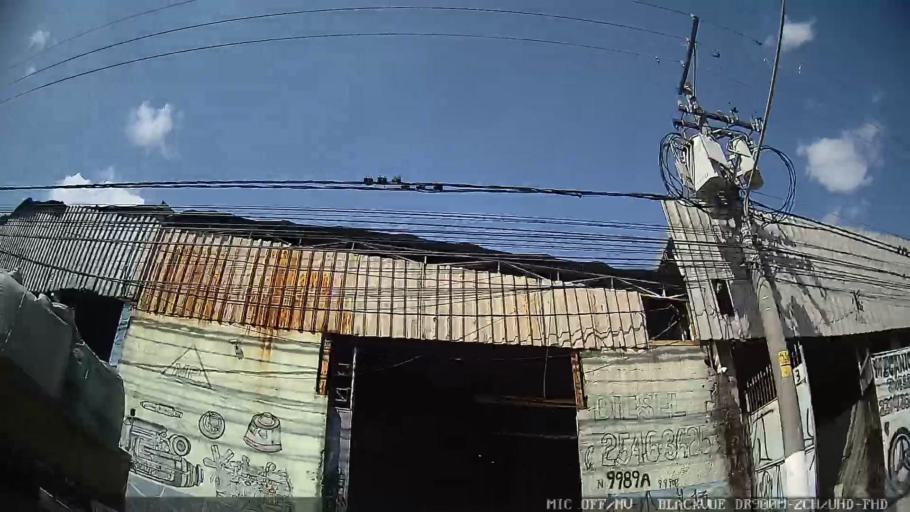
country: BR
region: Sao Paulo
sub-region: Guarulhos
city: Guarulhos
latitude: -23.4858
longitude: -46.4671
